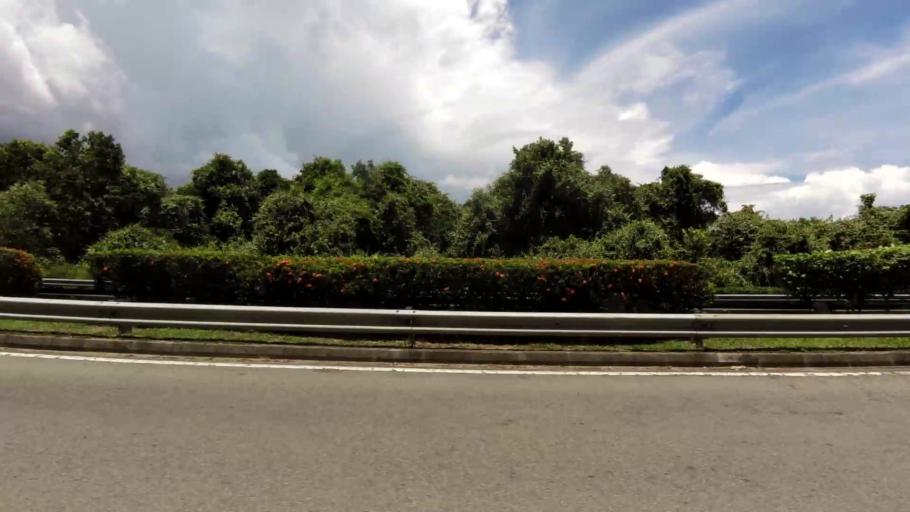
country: BN
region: Brunei and Muara
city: Bandar Seri Begawan
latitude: 4.9499
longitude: 114.9045
